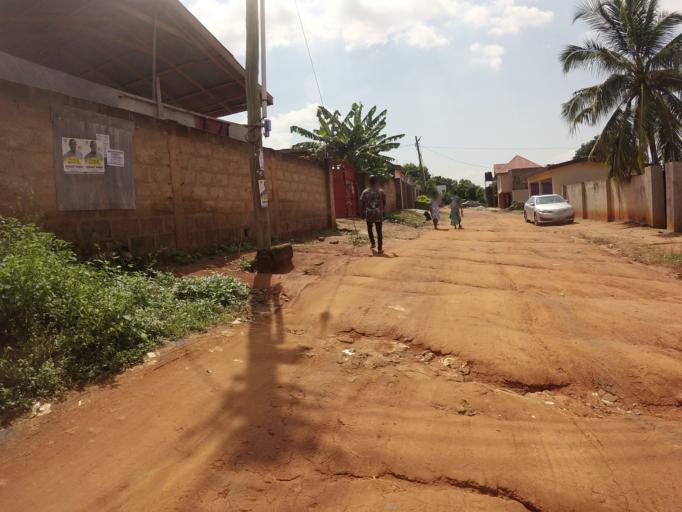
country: GH
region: Greater Accra
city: Gbawe
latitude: 5.6230
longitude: -0.3098
